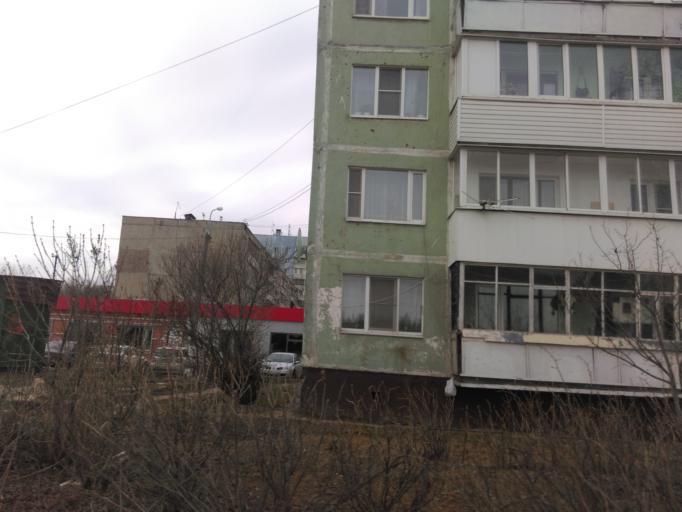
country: RU
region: Moskovskaya
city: Tuchkovo
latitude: 55.6023
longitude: 36.4904
